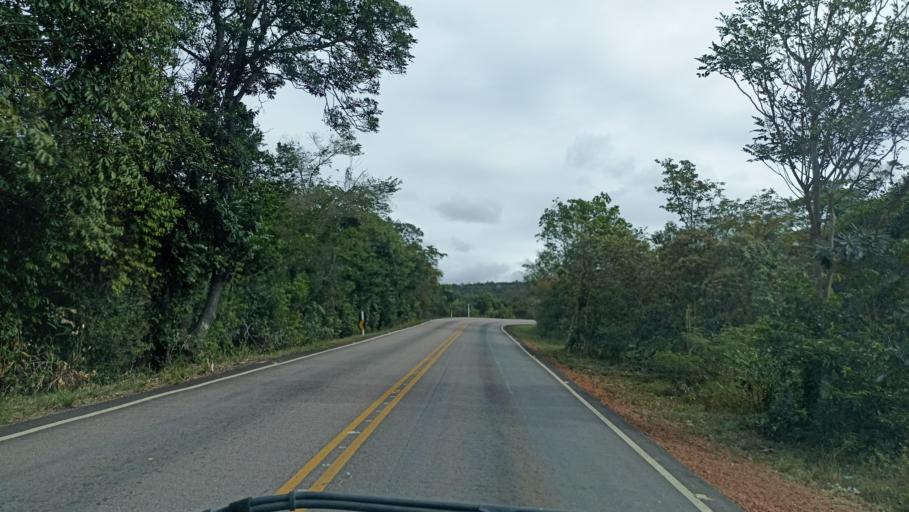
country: BR
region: Bahia
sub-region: Andarai
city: Vera Cruz
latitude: -12.9322
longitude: -41.2397
